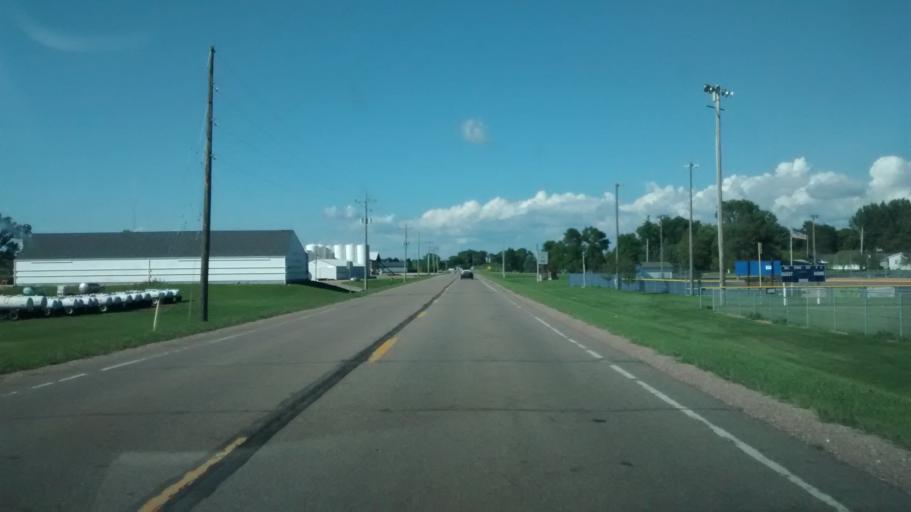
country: US
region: Iowa
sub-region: Woodbury County
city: Moville
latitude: 42.4909
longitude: -96.0742
